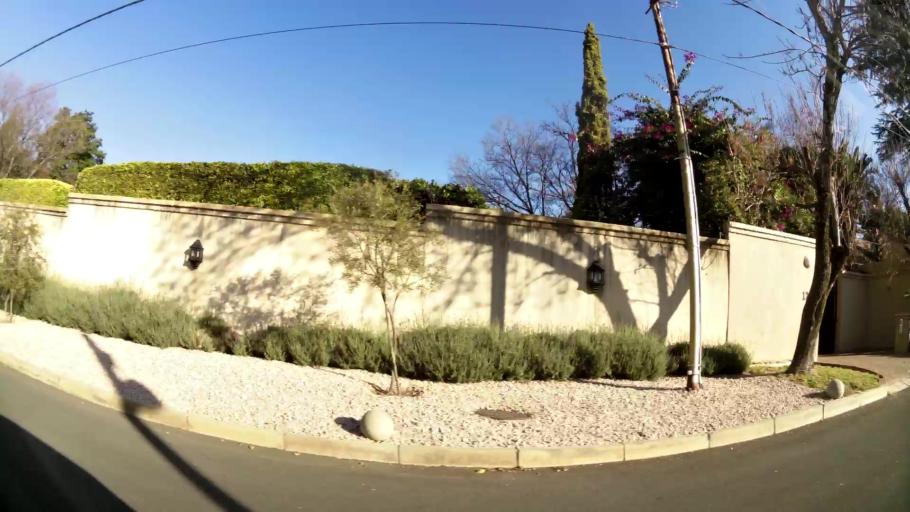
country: ZA
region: Gauteng
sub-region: City of Johannesburg Metropolitan Municipality
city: Johannesburg
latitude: -26.1138
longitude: 28.0687
